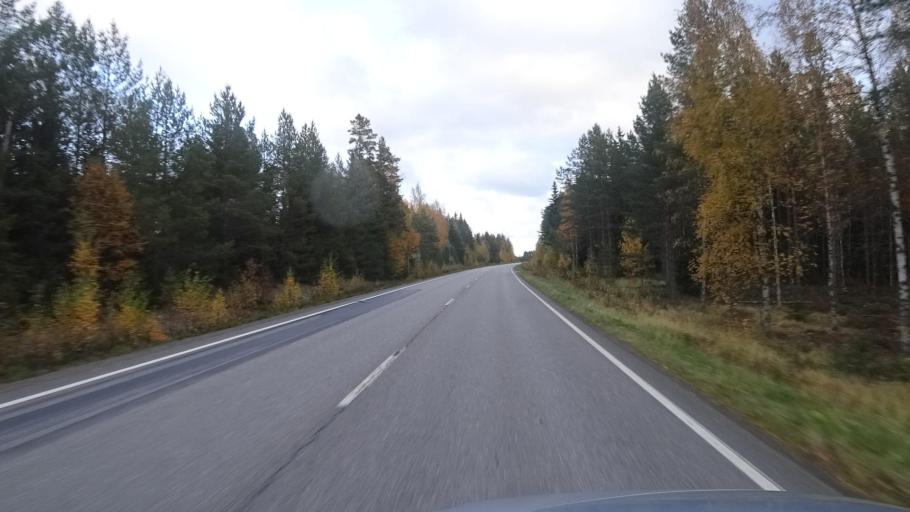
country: FI
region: Varsinais-Suomi
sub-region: Loimaa
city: Ylaene
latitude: 60.9961
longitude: 22.4985
